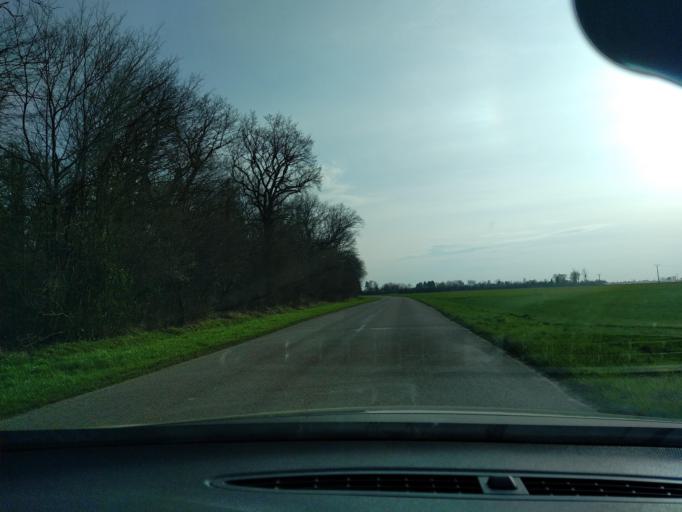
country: FR
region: Franche-Comte
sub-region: Departement du Jura
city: Choisey
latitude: 46.9979
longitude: 5.4714
